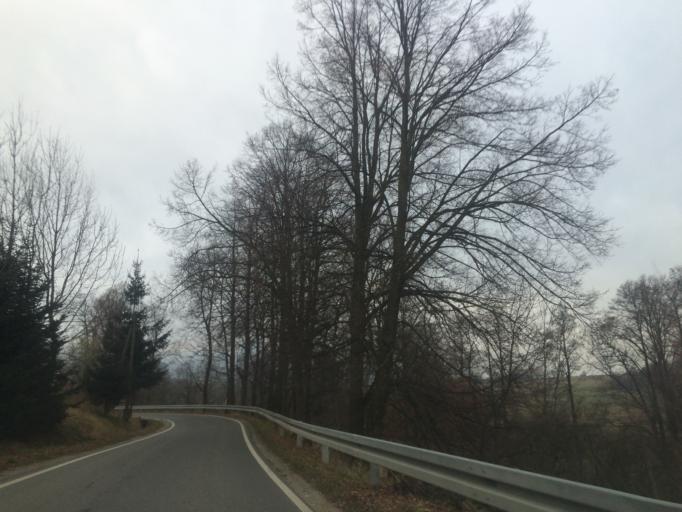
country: PL
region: Lower Silesian Voivodeship
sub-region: Powiat klodzki
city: Bystrzyca Klodzka
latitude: 50.2700
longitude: 16.7026
